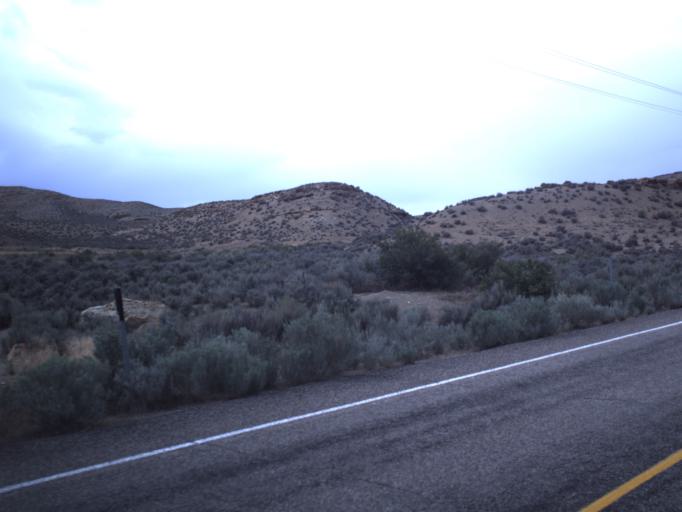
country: US
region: Colorado
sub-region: Rio Blanco County
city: Rangely
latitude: 39.9962
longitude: -109.1782
